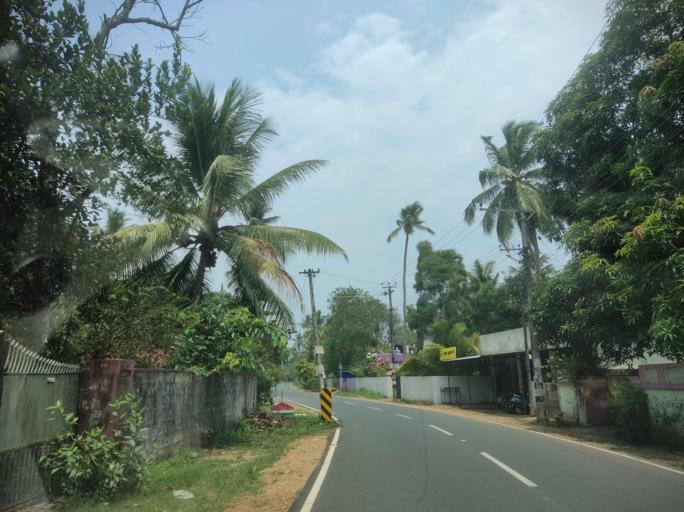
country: IN
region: Kerala
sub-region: Alappuzha
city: Vayalar
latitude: 9.7019
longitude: 76.3255
